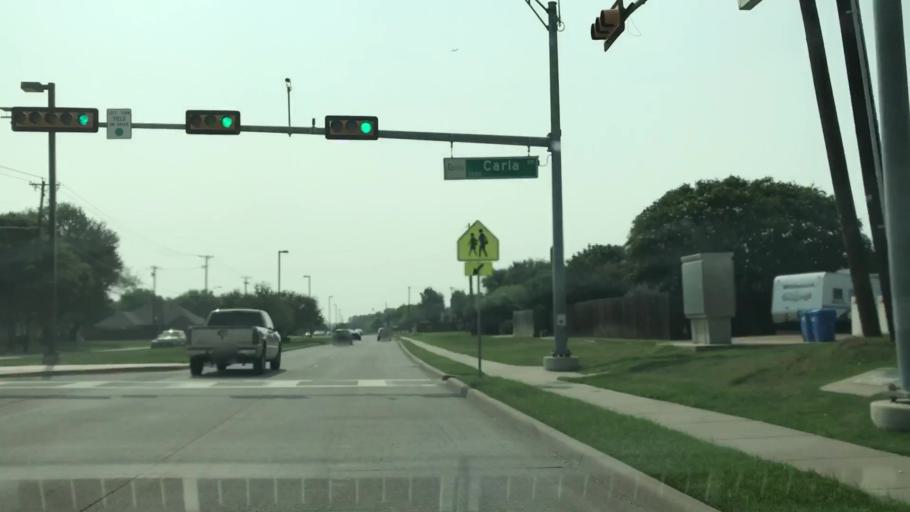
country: US
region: Texas
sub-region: Dallas County
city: Rowlett
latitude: 32.8940
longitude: -96.5746
